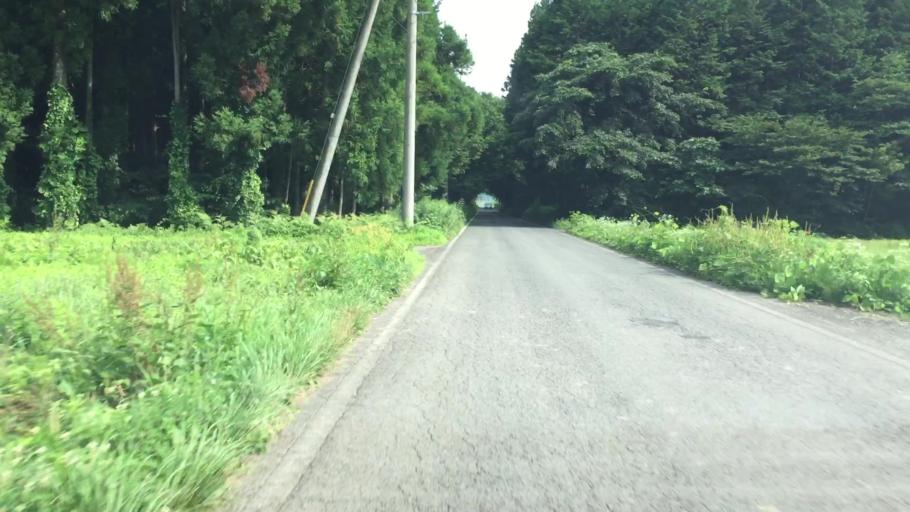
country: JP
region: Tochigi
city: Kuroiso
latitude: 37.0192
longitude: 139.9484
